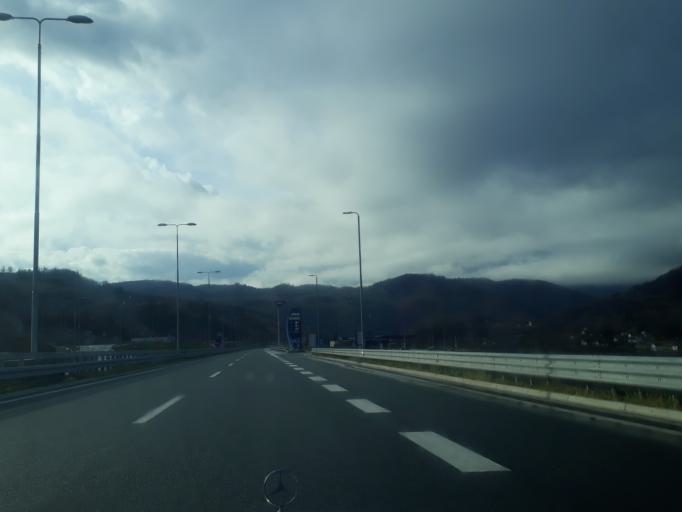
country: BA
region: Federation of Bosnia and Herzegovina
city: Polje
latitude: 43.8451
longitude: 18.1270
